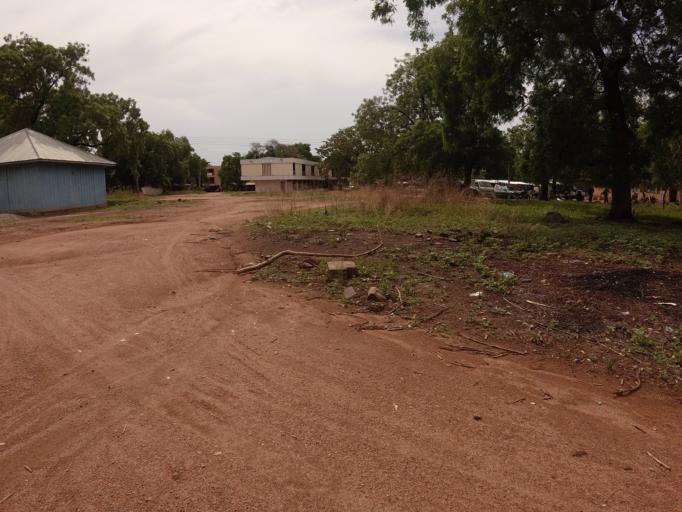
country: GH
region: Upper East
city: Bolgatanga
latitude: 10.7953
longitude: -0.8567
